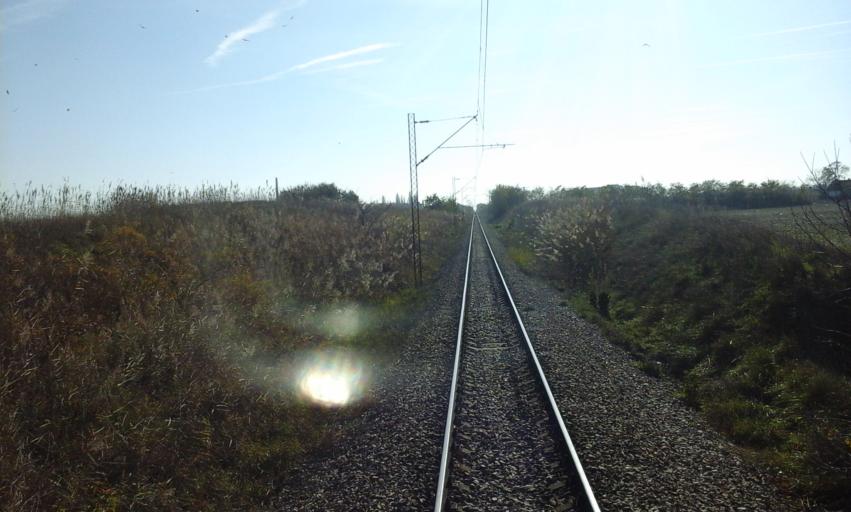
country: RS
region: Autonomna Pokrajina Vojvodina
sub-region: Severnobacki Okrug
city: Subotica
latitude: 46.0787
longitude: 19.6897
